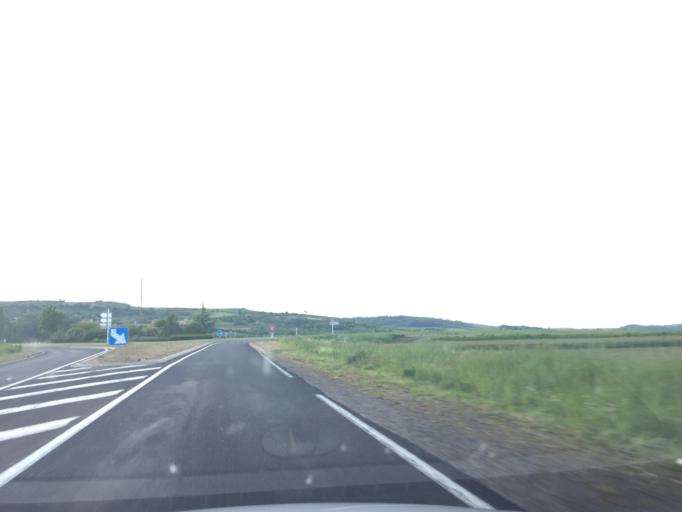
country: FR
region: Auvergne
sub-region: Departement du Puy-de-Dome
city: Chatel-Guyon
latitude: 45.9257
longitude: 3.0846
